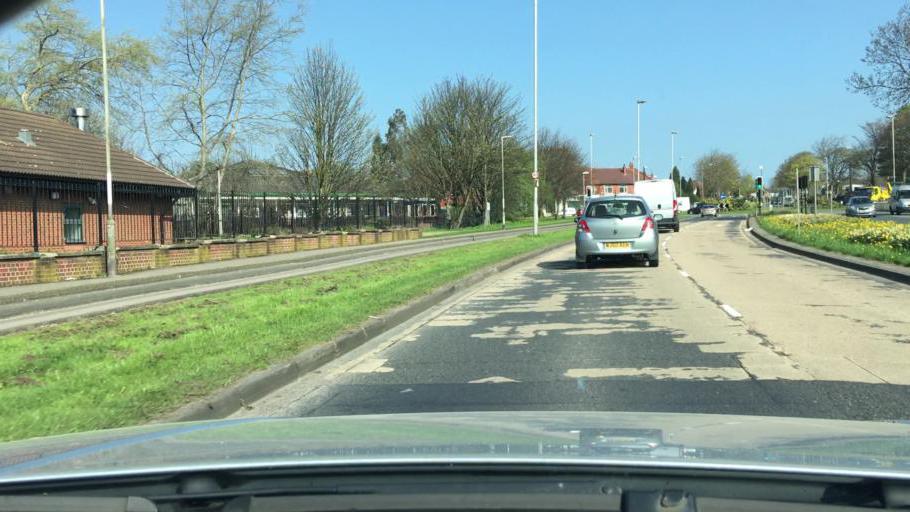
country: GB
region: England
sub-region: City and Borough of Leeds
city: Chapel Allerton
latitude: 53.8238
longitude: -1.5454
